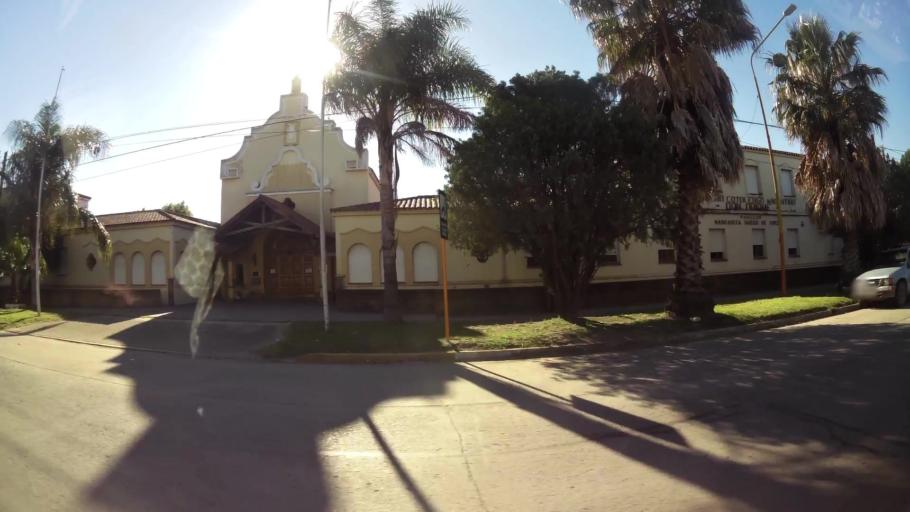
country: AR
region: Cordoba
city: San Francisco
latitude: -31.4189
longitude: -62.0950
